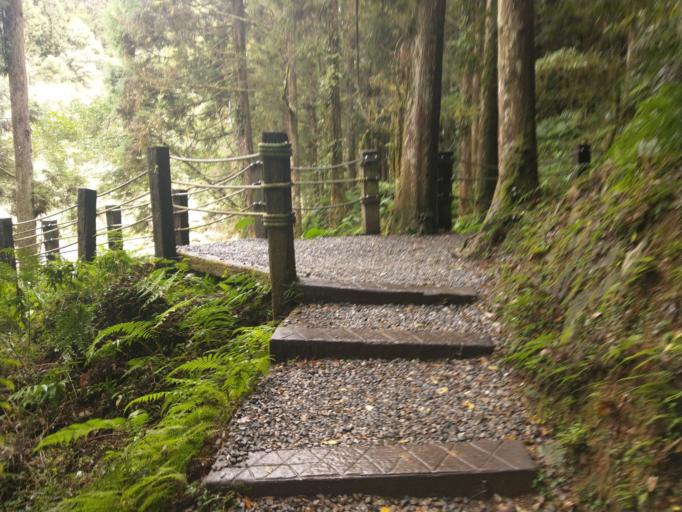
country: TW
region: Taiwan
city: Lugu
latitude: 23.6305
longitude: 120.7955
